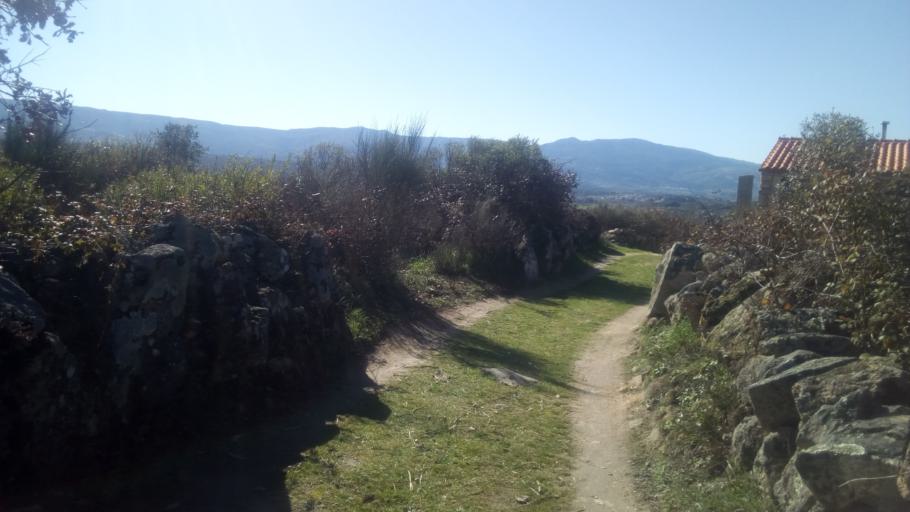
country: PT
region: Guarda
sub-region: Fornos de Algodres
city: Fornos de Algodres
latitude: 40.6029
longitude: -7.5070
